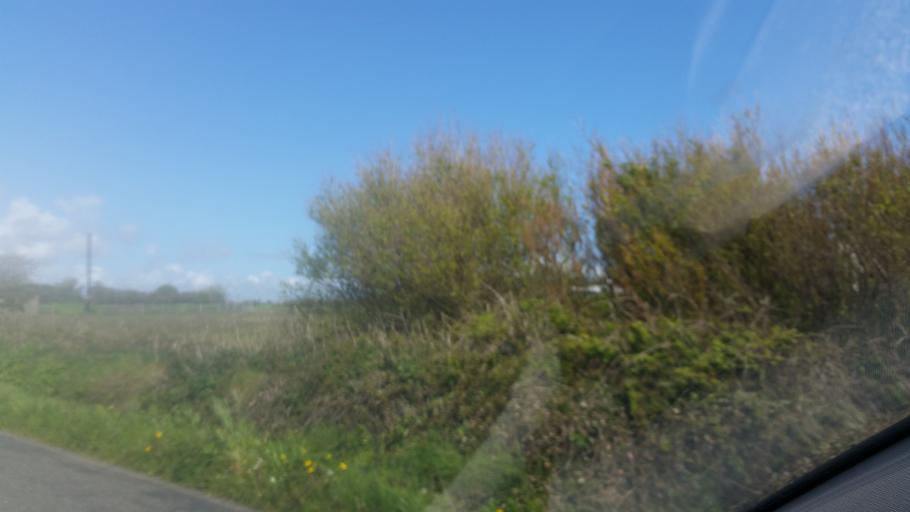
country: IE
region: Munster
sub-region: Waterford
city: Dunmore East
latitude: 52.1608
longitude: -6.8941
